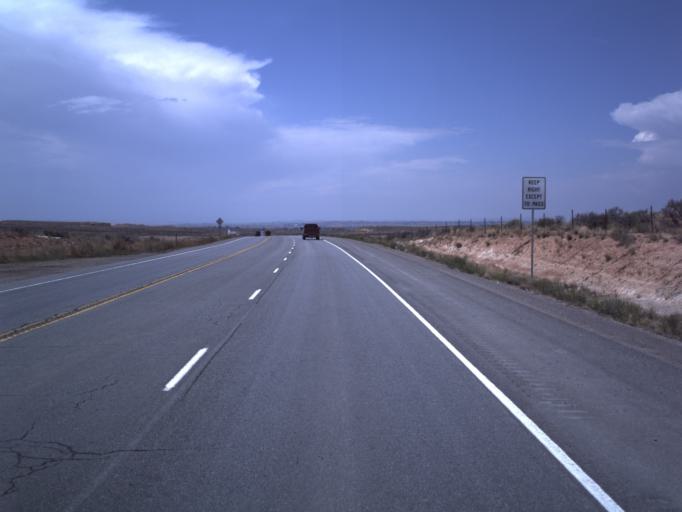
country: US
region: Utah
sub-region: Uintah County
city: Maeser
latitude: 40.3145
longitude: -109.7376
